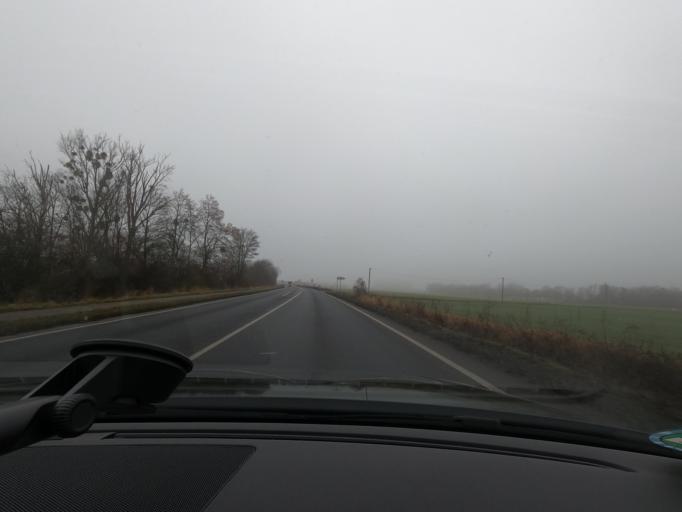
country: DE
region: North Rhine-Westphalia
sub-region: Regierungsbezirk Koln
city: Dueren
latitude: 50.7755
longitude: 6.5162
